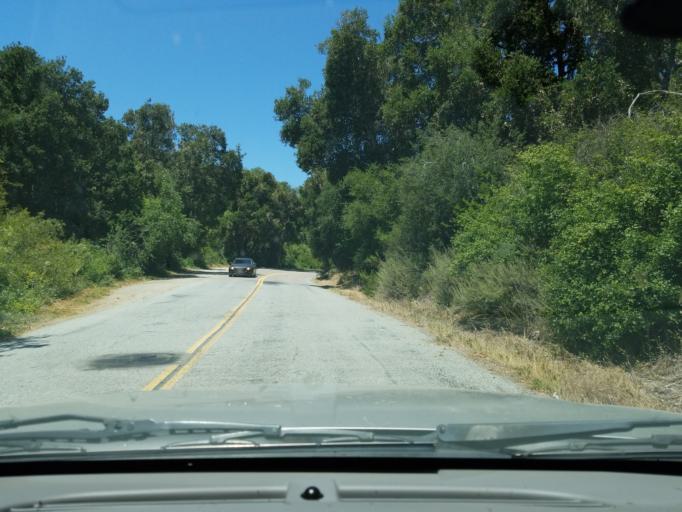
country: US
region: California
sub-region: Monterey County
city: Carmel Valley Village
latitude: 36.4481
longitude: -121.6842
